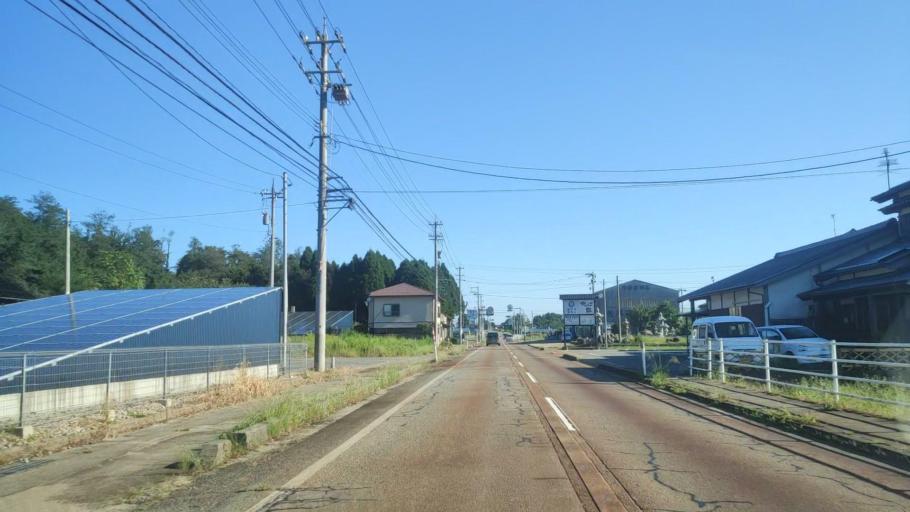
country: JP
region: Ishikawa
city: Hakui
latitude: 36.8131
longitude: 136.7559
